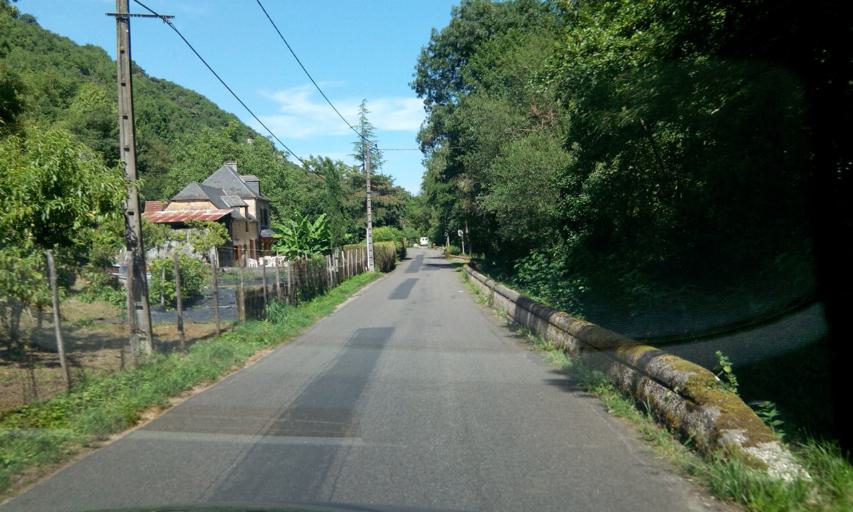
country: FR
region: Midi-Pyrenees
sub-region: Departement du Lot
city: Vayrac
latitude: 44.9312
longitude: 1.6497
